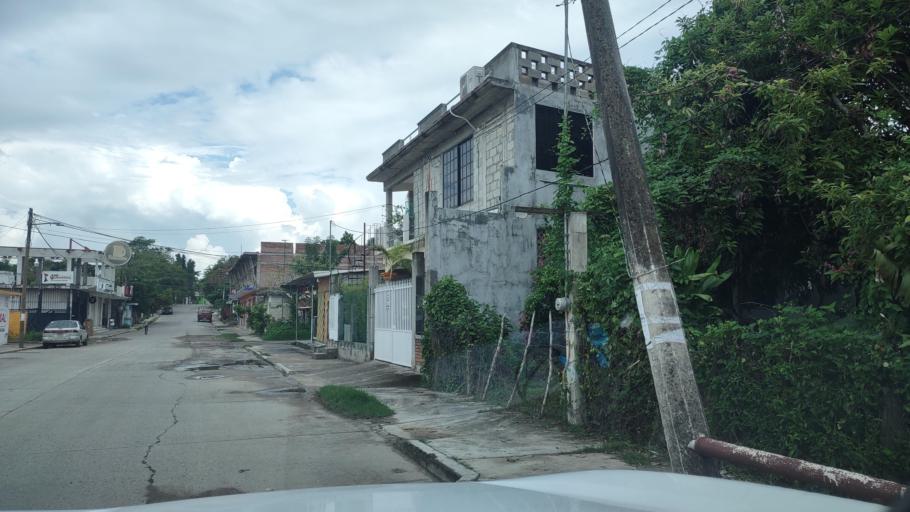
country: MX
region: Veracruz
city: Tuxpan de Rodriguez Cano
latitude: 20.9550
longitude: -97.4225
